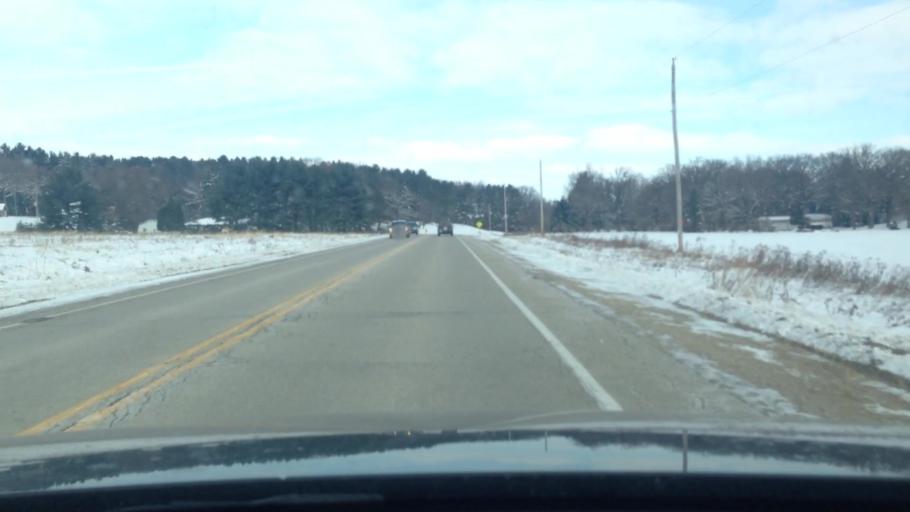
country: US
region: Wisconsin
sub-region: Walworth County
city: Lake Geneva
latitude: 42.6292
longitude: -88.4137
